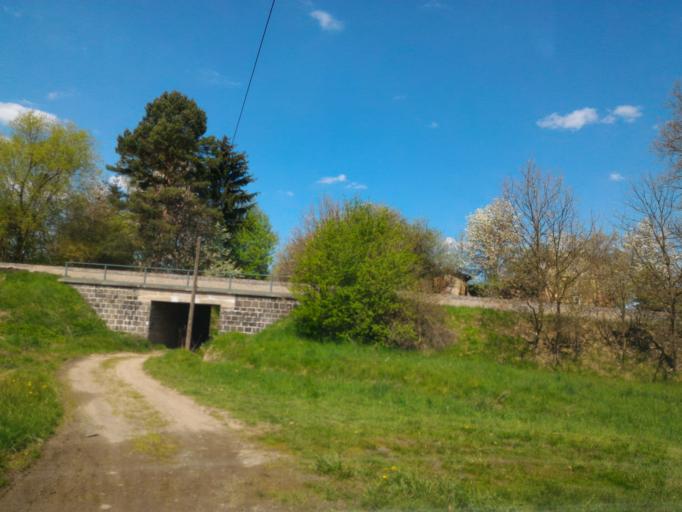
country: DE
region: Saxony
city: Eibau
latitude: 50.9665
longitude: 14.6708
